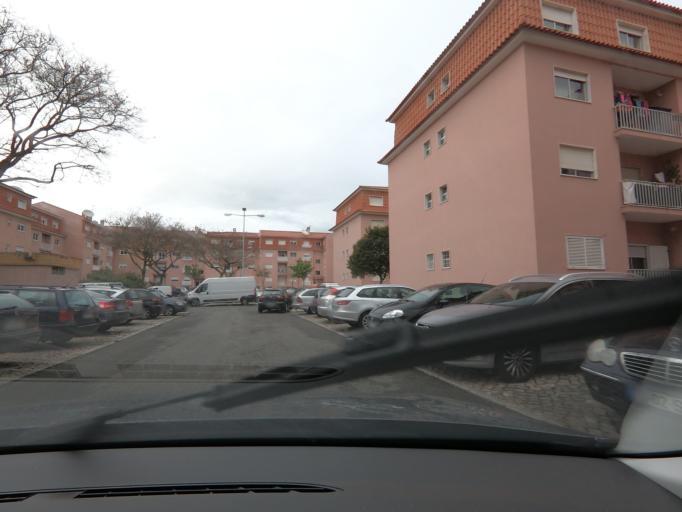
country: PT
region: Lisbon
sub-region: Cascais
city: Sao Domingos de Rana
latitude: 38.7253
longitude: -9.3310
